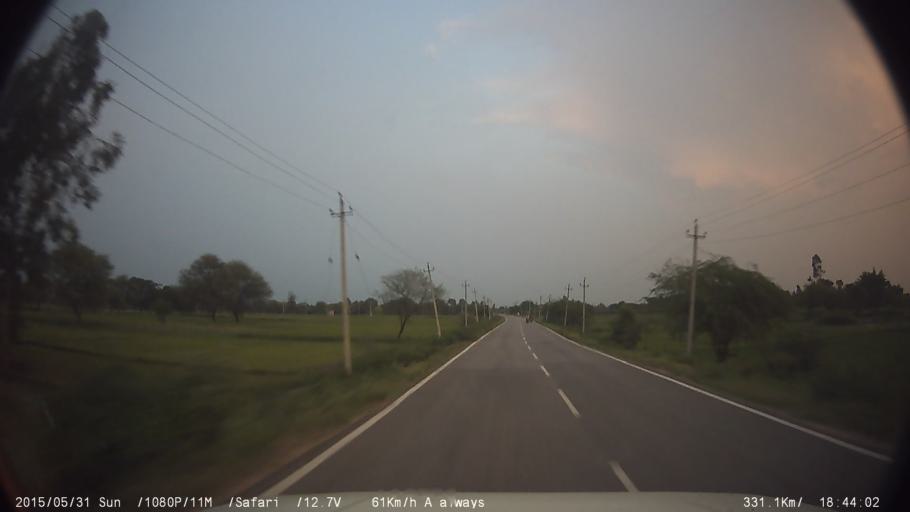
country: IN
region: Karnataka
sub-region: Mysore
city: Tirumakudal Narsipur
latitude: 12.1569
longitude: 76.8120
